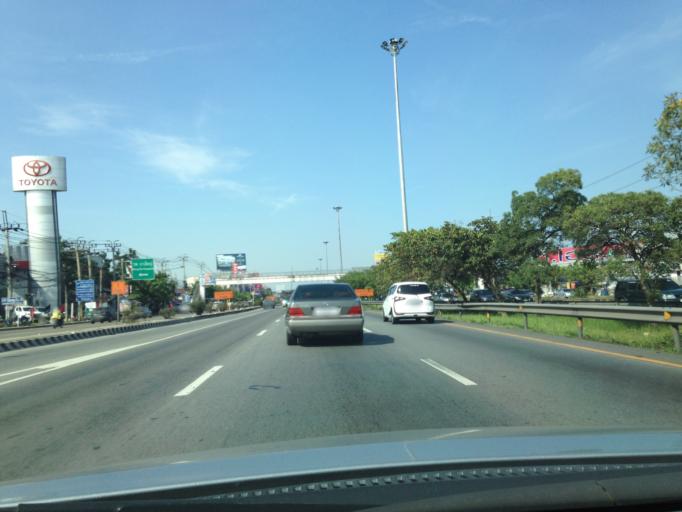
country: TH
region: Nonthaburi
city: Bang Yai
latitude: 13.8434
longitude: 100.4128
